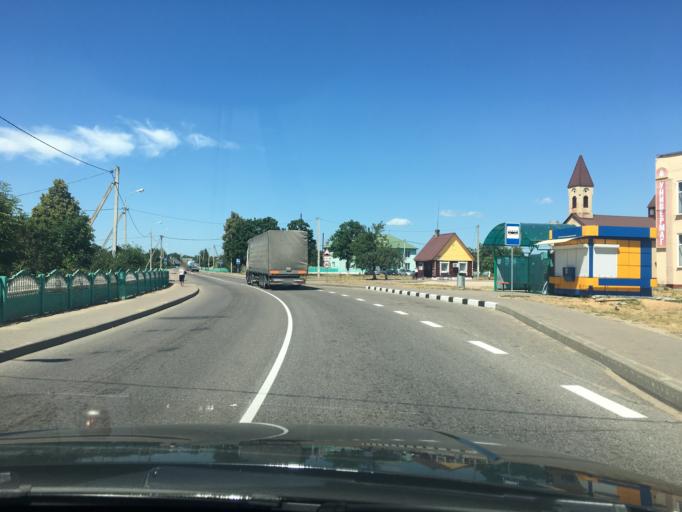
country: BY
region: Grodnenskaya
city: Iwye
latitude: 54.0323
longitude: 25.9266
